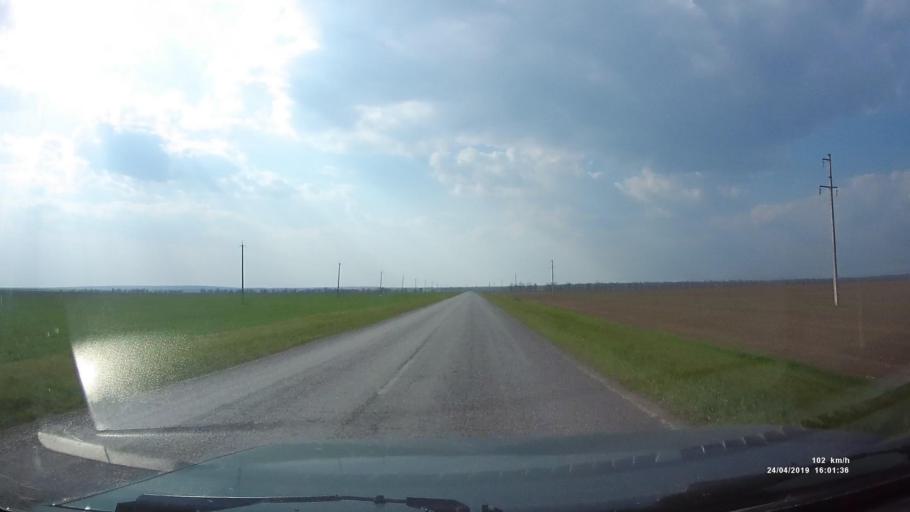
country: RU
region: Rostov
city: Sovetskoye
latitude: 46.6432
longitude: 42.4332
